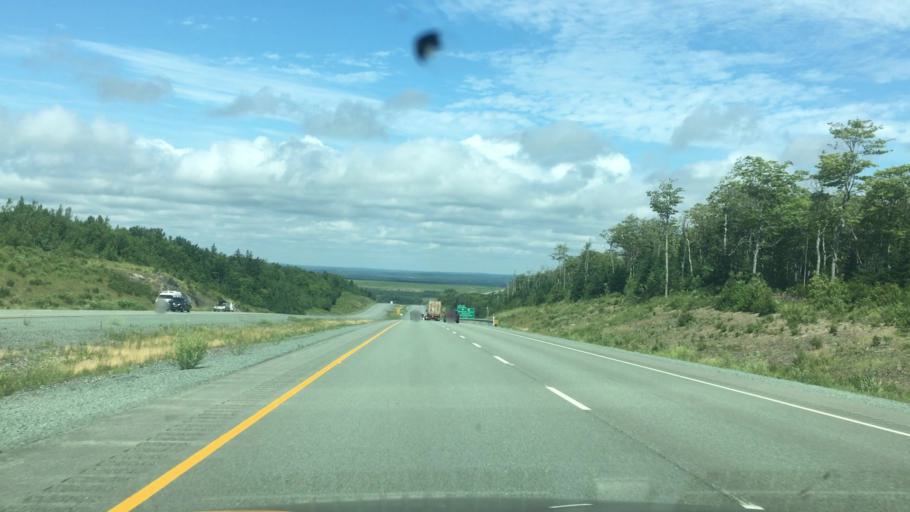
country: CA
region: Nova Scotia
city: Oxford
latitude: 45.5869
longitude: -63.7203
